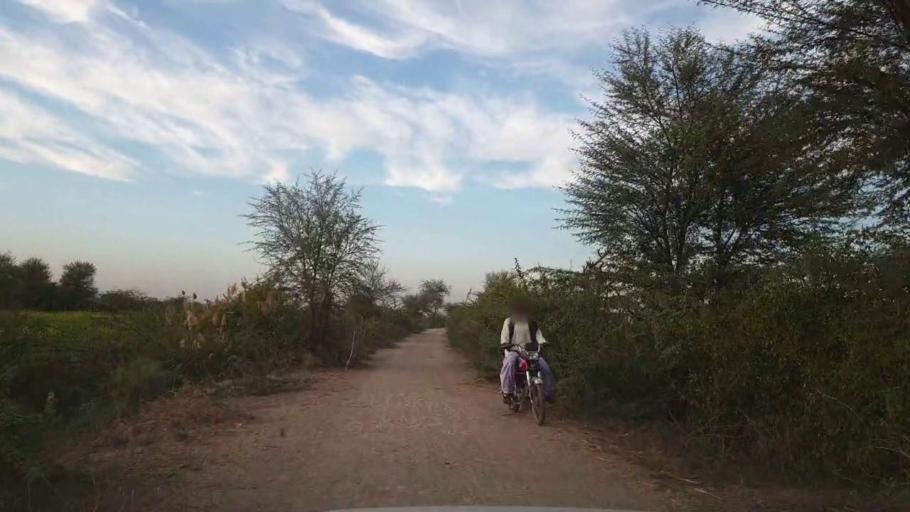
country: PK
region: Sindh
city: Pithoro
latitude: 25.6053
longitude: 69.2033
